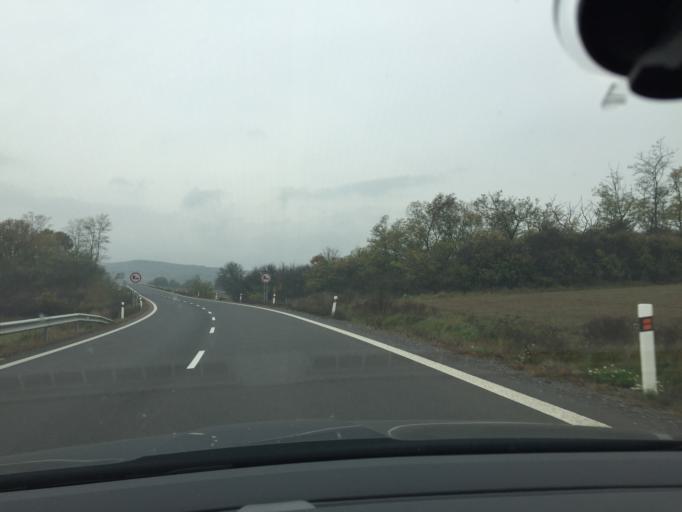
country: SK
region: Banskobystricky
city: Velky Krtis
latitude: 48.2241
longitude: 19.3966
